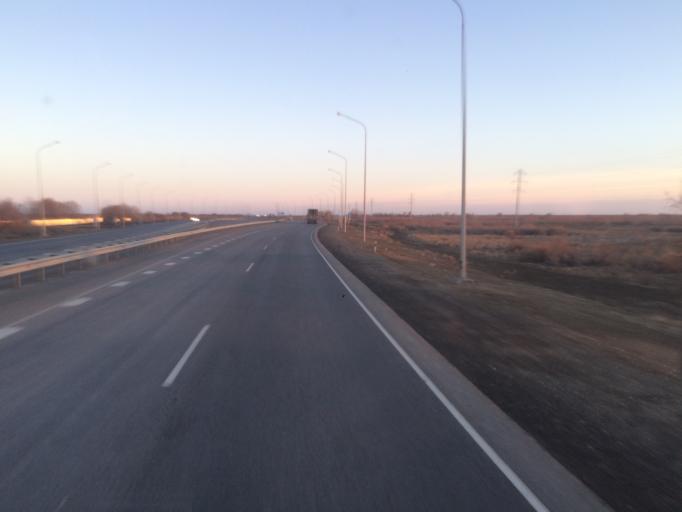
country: KZ
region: Qyzylorda
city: Shieli
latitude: 44.1331
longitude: 66.9761
